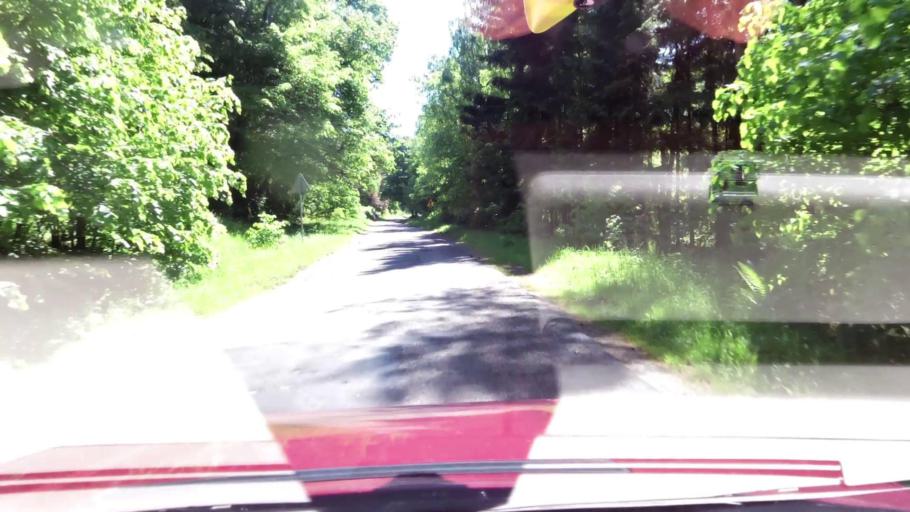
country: PL
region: West Pomeranian Voivodeship
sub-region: Powiat koszalinski
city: Bobolice
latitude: 54.0507
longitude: 16.5850
